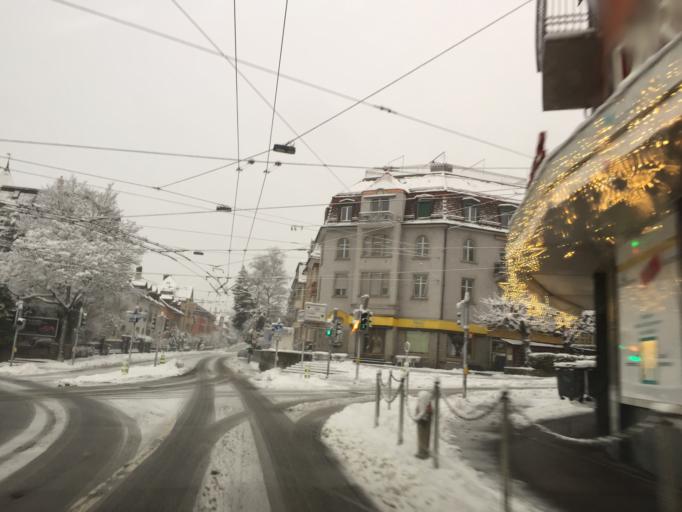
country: CH
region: Zurich
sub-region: Bezirk Zuerich
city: Zuerich (Kreis 7) / Hirslanden
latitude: 47.3644
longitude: 8.5666
